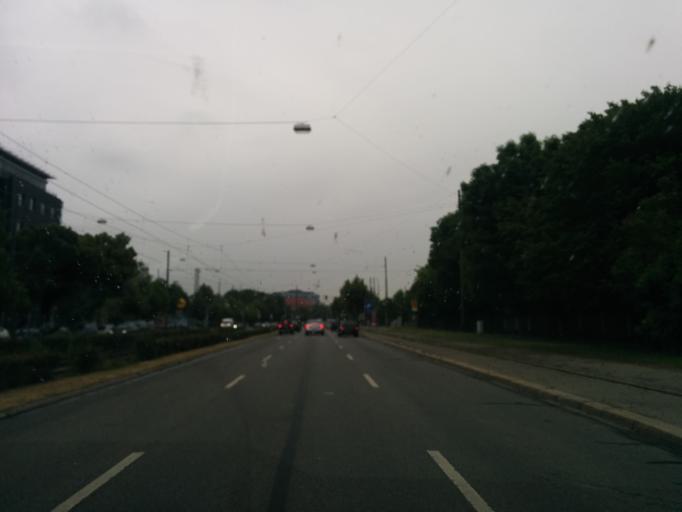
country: DE
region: Bavaria
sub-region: Upper Bavaria
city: Munich
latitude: 48.1731
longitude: 11.5267
